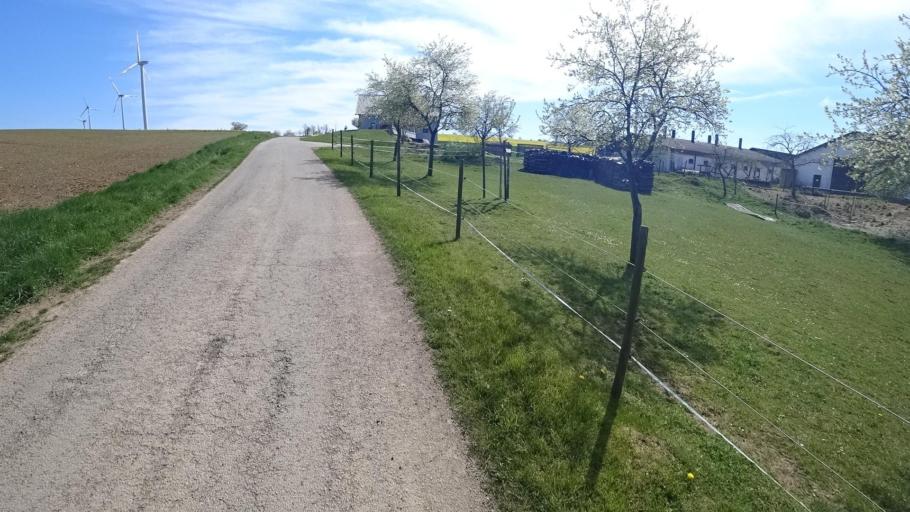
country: DE
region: Rheinland-Pfalz
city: Eisenach
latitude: 49.8479
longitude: 6.5150
